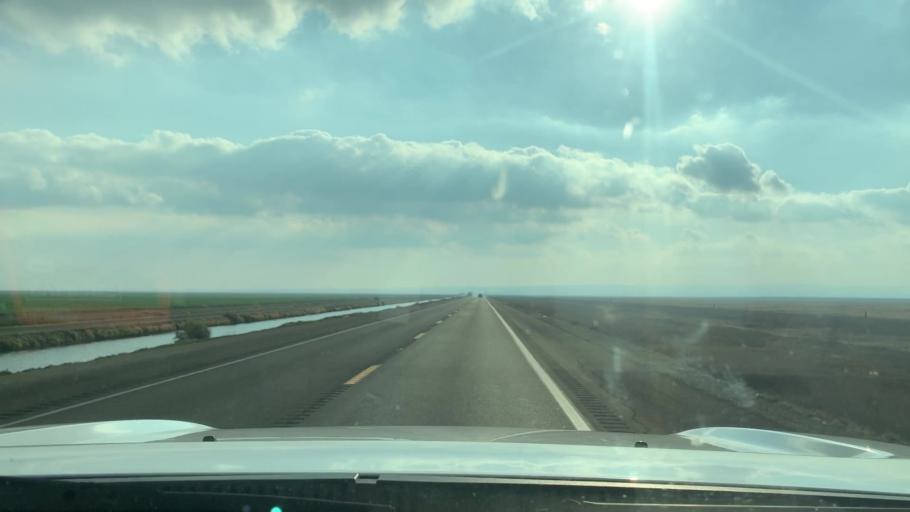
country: US
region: California
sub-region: Kings County
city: Stratford
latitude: 36.1188
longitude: -119.8951
